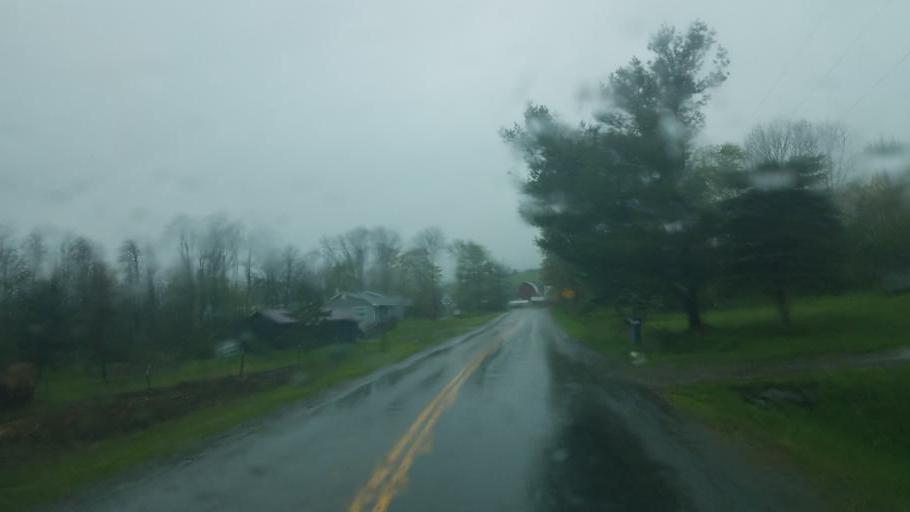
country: US
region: Pennsylvania
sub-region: Tioga County
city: Westfield
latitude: 42.0823
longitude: -77.5029
